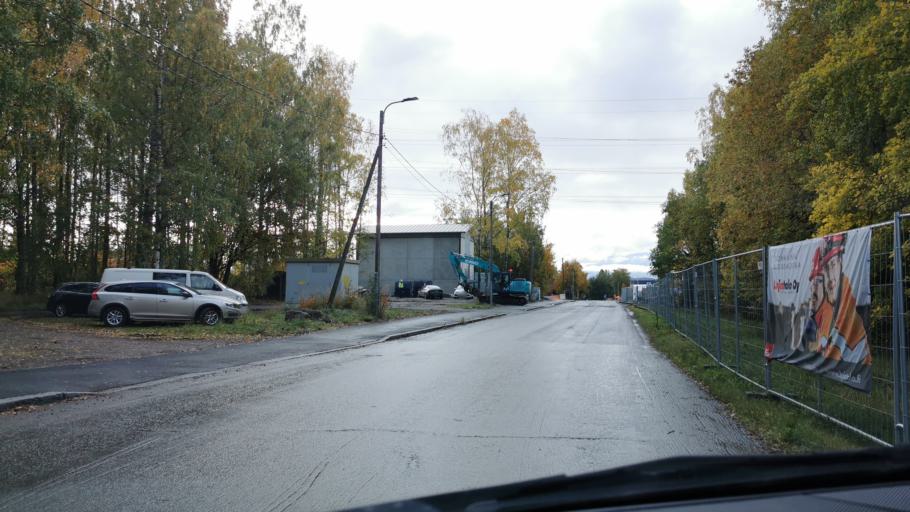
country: FI
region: Ostrobothnia
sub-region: Vaasa
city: Vaasa
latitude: 63.0925
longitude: 21.5634
